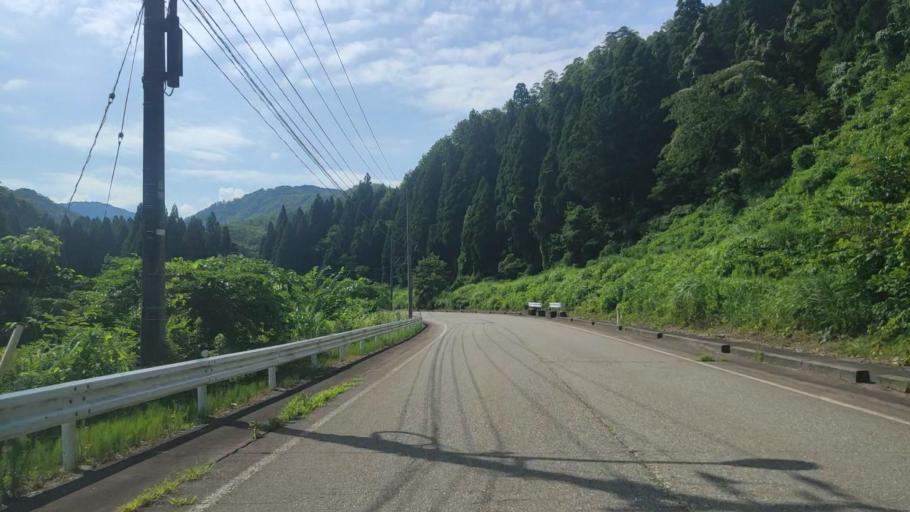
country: JP
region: Ishikawa
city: Komatsu
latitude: 36.3241
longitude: 136.5301
